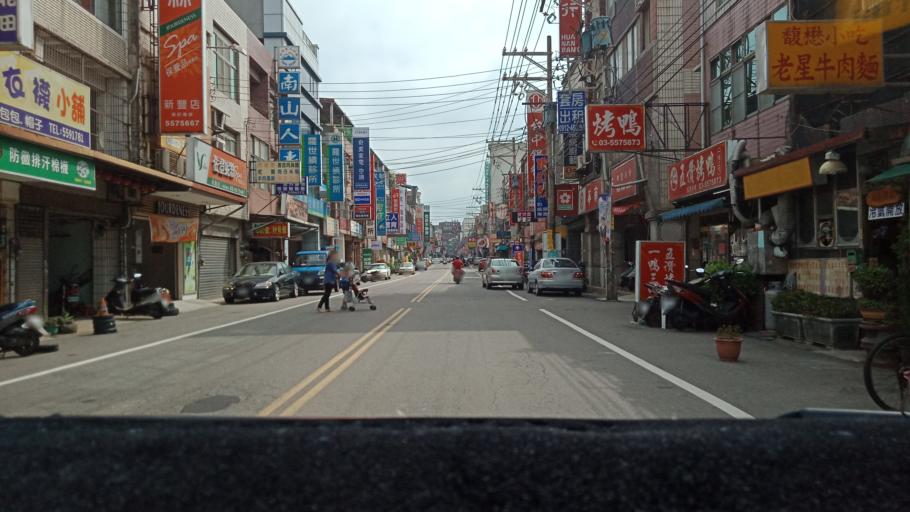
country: TW
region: Taiwan
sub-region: Hsinchu
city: Zhubei
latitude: 24.8752
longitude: 120.9944
